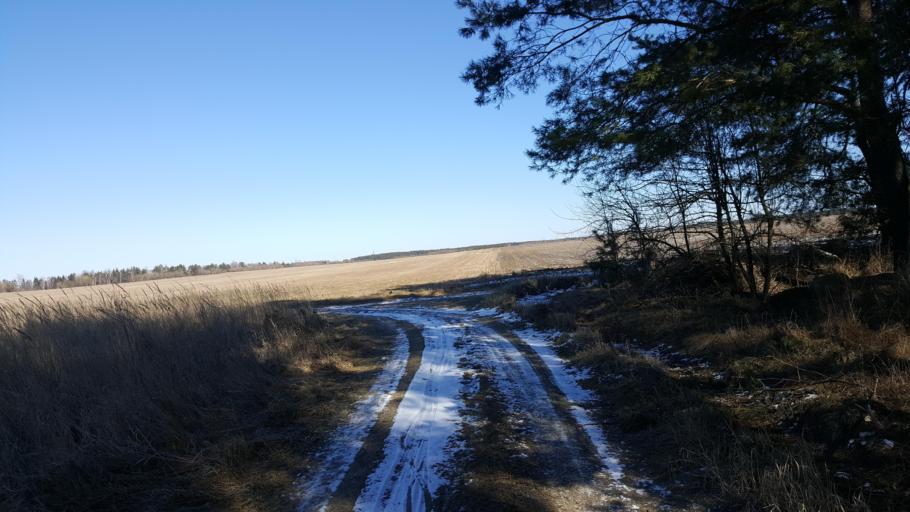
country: BY
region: Brest
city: Kamyanyets
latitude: 52.3732
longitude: 23.8065
